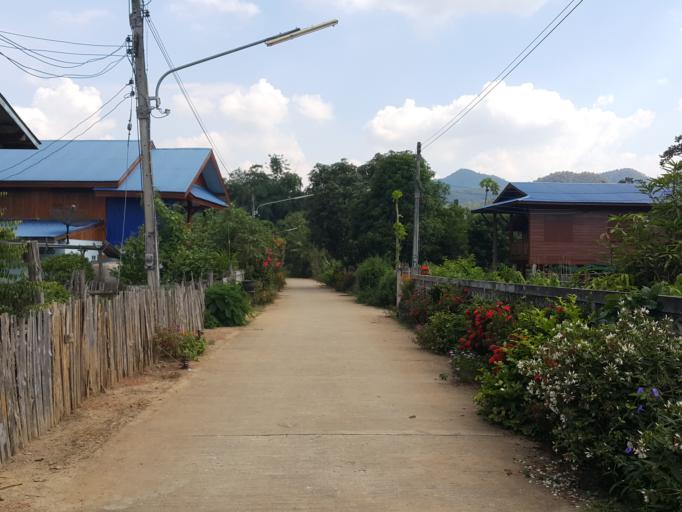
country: TH
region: Sukhothai
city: Thung Saliam
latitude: 17.3283
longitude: 99.4569
